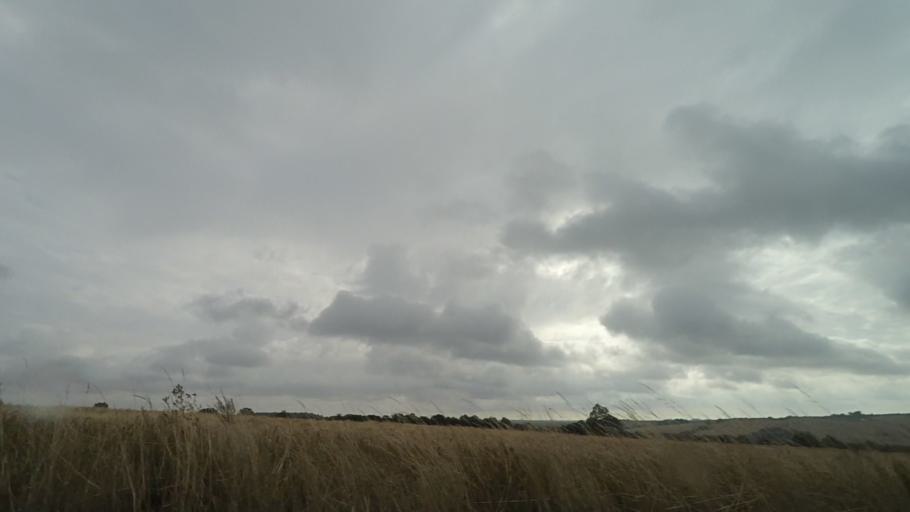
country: DK
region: Central Jutland
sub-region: Syddjurs Kommune
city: Ronde
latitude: 56.3203
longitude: 10.4592
